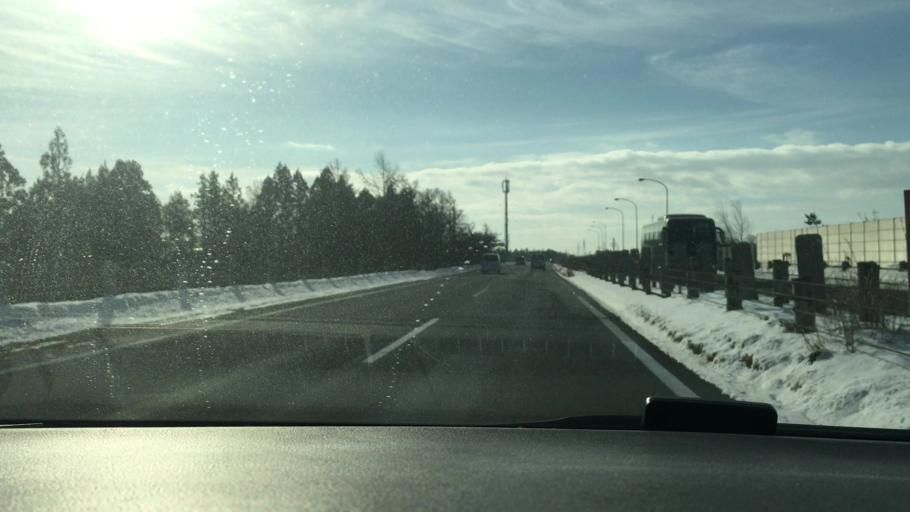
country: JP
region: Iwate
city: Hanamaki
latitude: 39.3454
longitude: 141.0907
